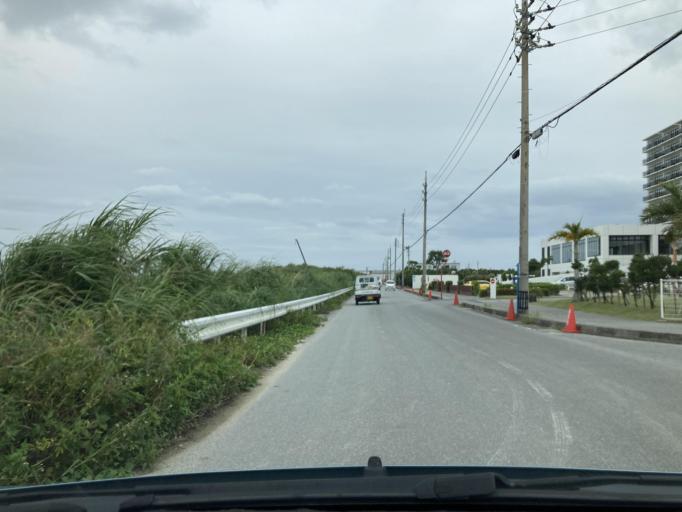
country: JP
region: Okinawa
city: Itoman
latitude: 26.1330
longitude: 127.6535
